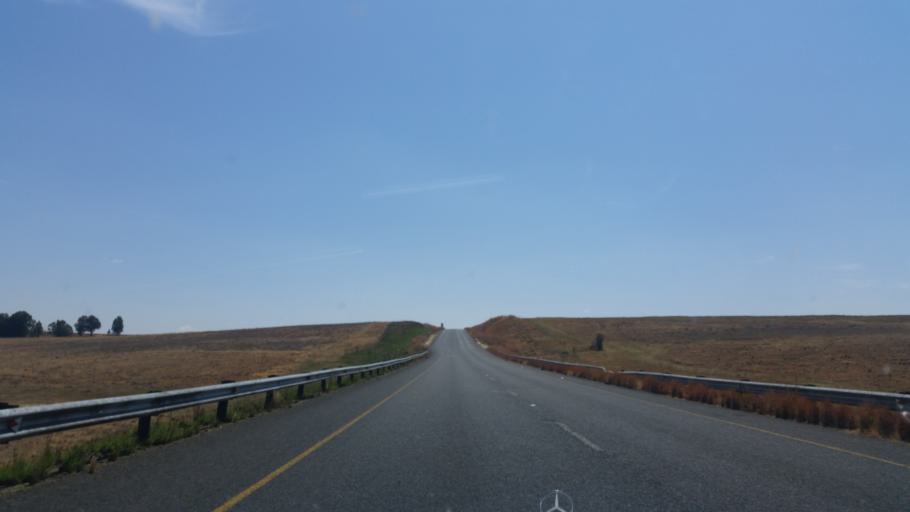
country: ZA
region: Orange Free State
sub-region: Thabo Mofutsanyana District Municipality
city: Phuthaditjhaba
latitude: -28.1750
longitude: 28.6845
